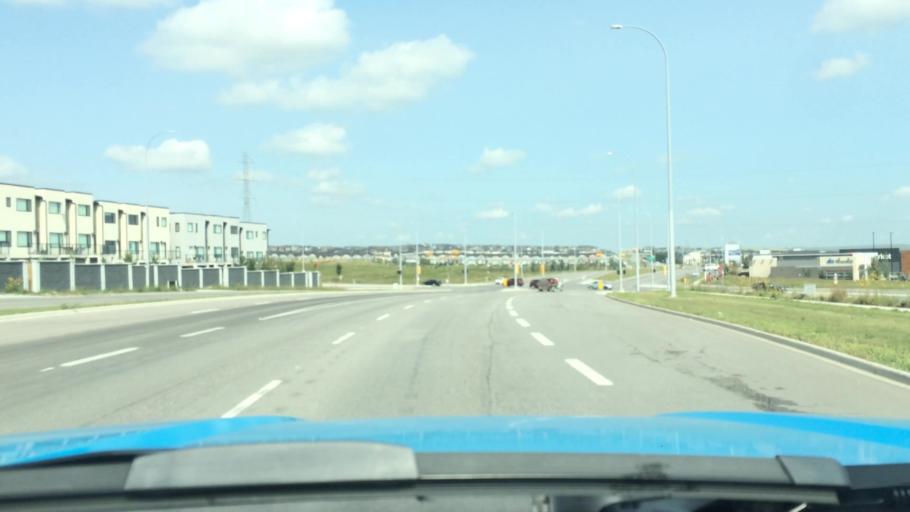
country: CA
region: Alberta
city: Calgary
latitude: 51.1668
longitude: -114.1508
